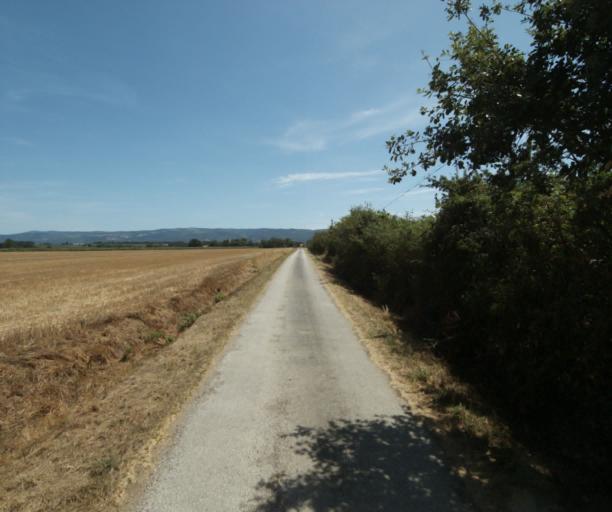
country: FR
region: Midi-Pyrenees
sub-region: Departement de la Haute-Garonne
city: Revel
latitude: 43.5028
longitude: 2.0241
